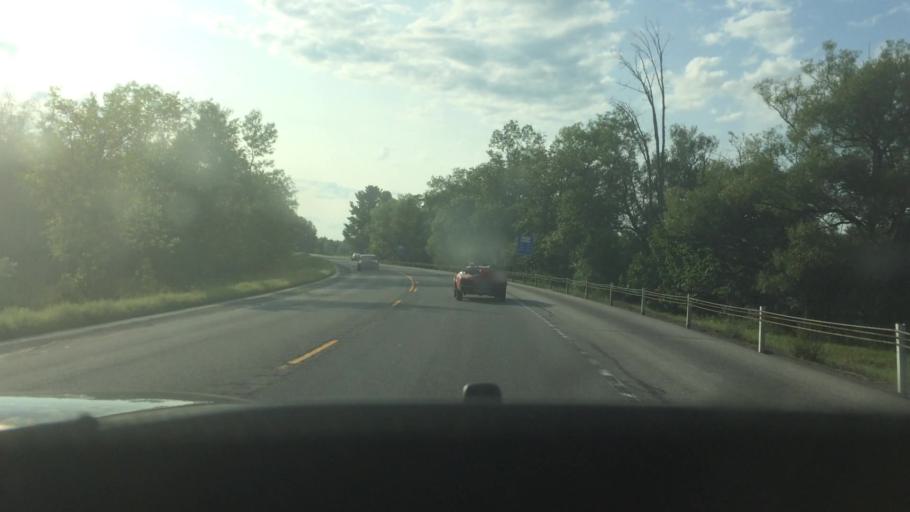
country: US
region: New York
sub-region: St. Lawrence County
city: Canton
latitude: 44.6187
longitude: -75.2232
